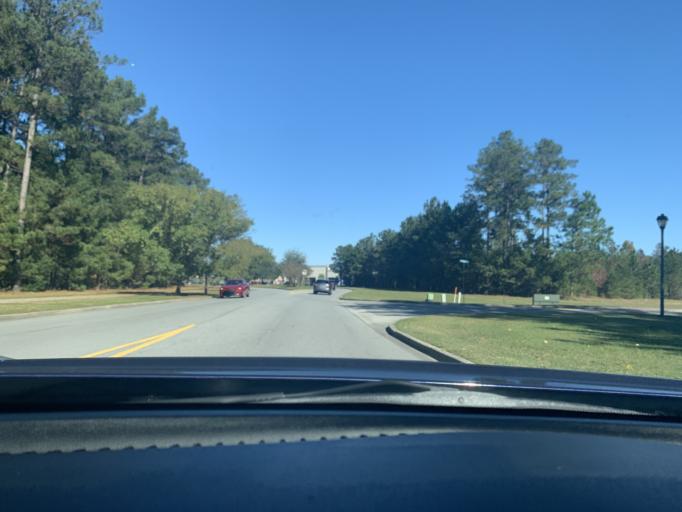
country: US
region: Georgia
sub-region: Chatham County
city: Pooler
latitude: 32.1378
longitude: -81.2561
